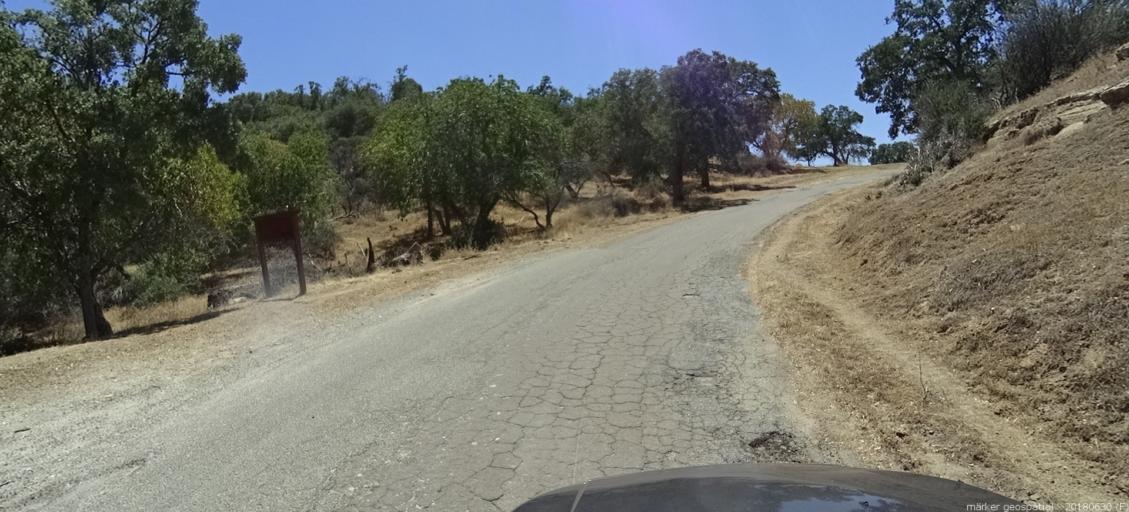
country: US
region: California
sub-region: Fresno County
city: Auberry
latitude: 37.1602
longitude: -119.4441
